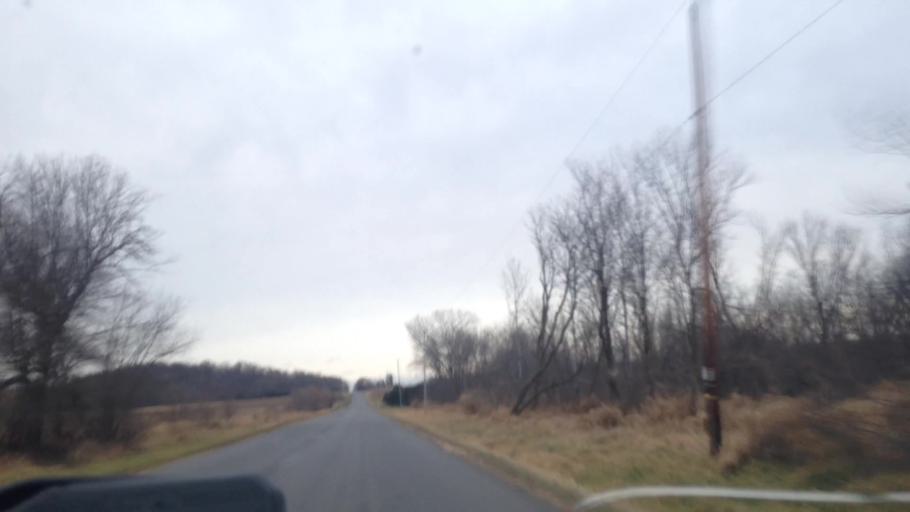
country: US
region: Wisconsin
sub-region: Dodge County
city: Theresa
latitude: 43.4859
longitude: -88.4644
